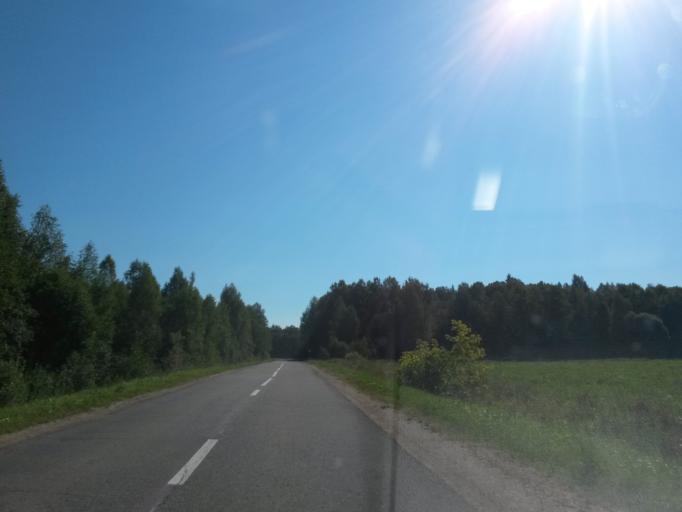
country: RU
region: Jaroslavl
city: Gavrilov-Yam
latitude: 57.3008
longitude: 40.0366
